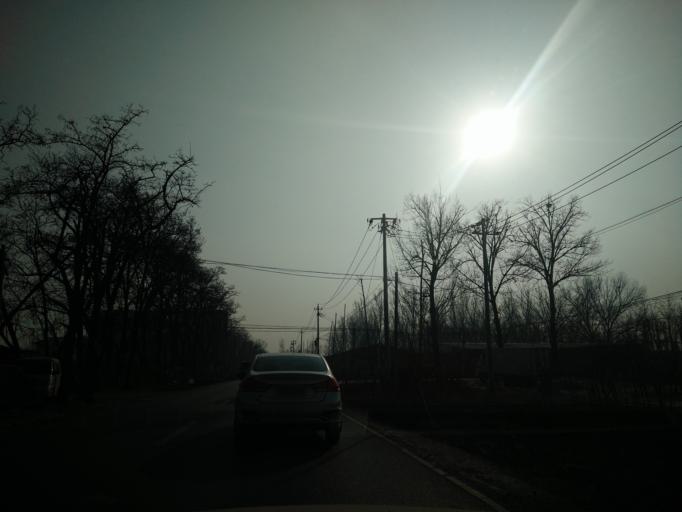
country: CN
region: Beijing
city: Xingfeng
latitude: 39.7283
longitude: 116.3722
